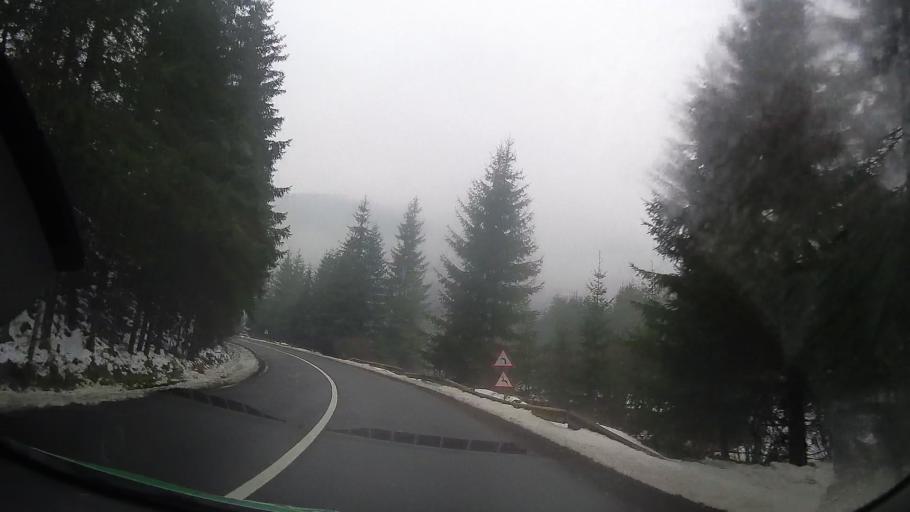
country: RO
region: Harghita
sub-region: Municipiul Gheorgheni
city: Gheorgheni
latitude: 46.7578
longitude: 25.6987
